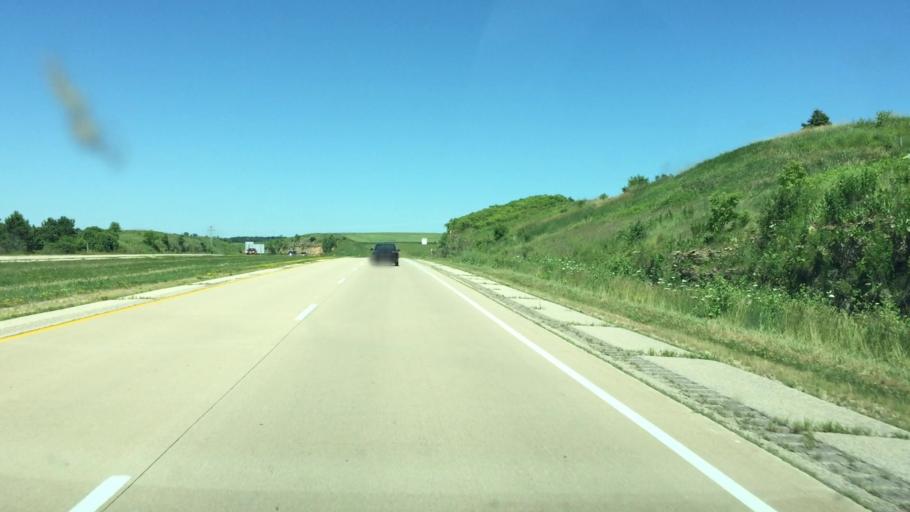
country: US
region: Wisconsin
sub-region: Iowa County
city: Mineral Point
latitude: 42.8644
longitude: -90.1996
